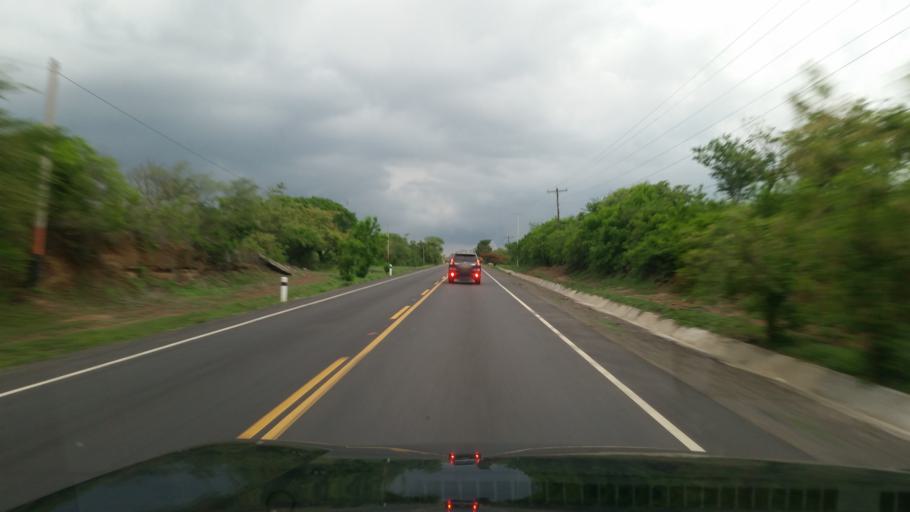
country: NI
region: Leon
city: Nagarote
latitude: 12.2689
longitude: -86.5527
